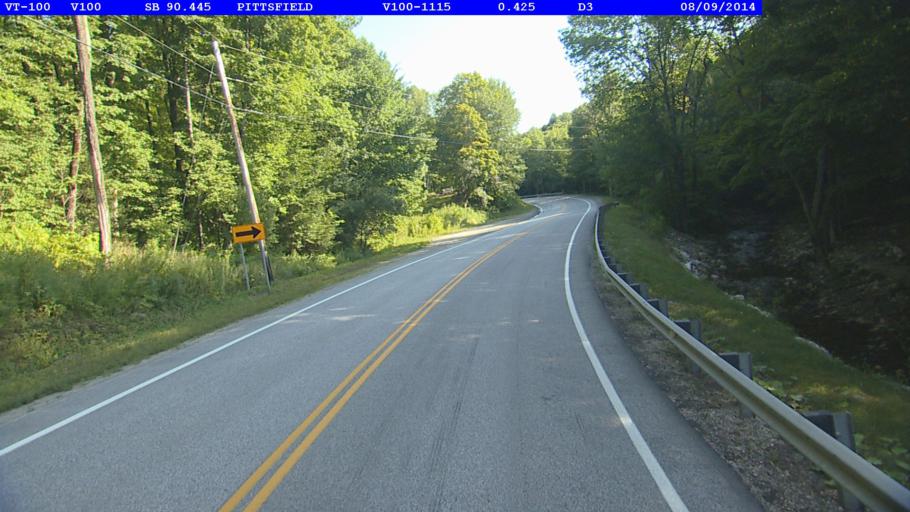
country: US
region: Vermont
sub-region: Rutland County
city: Rutland
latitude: 43.7236
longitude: -72.8226
